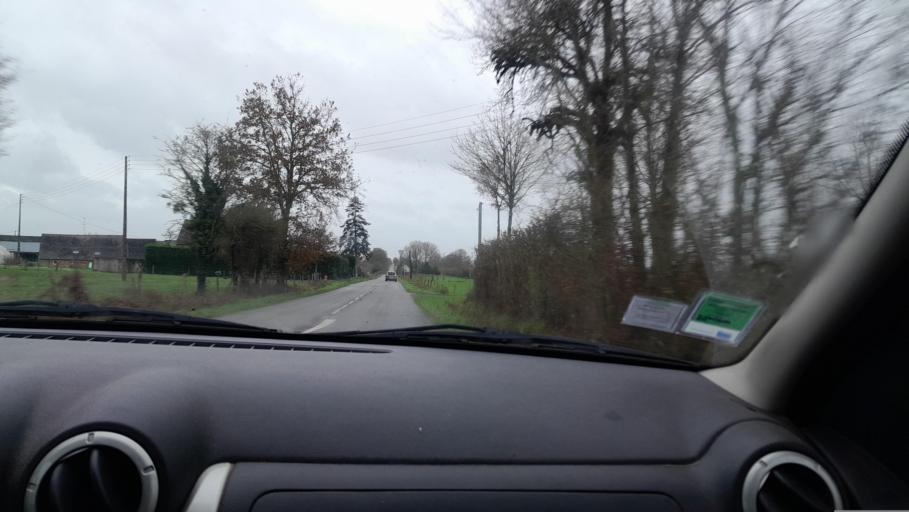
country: FR
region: Pays de la Loire
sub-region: Departement de la Mayenne
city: Ballots
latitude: 47.9348
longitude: -1.0885
